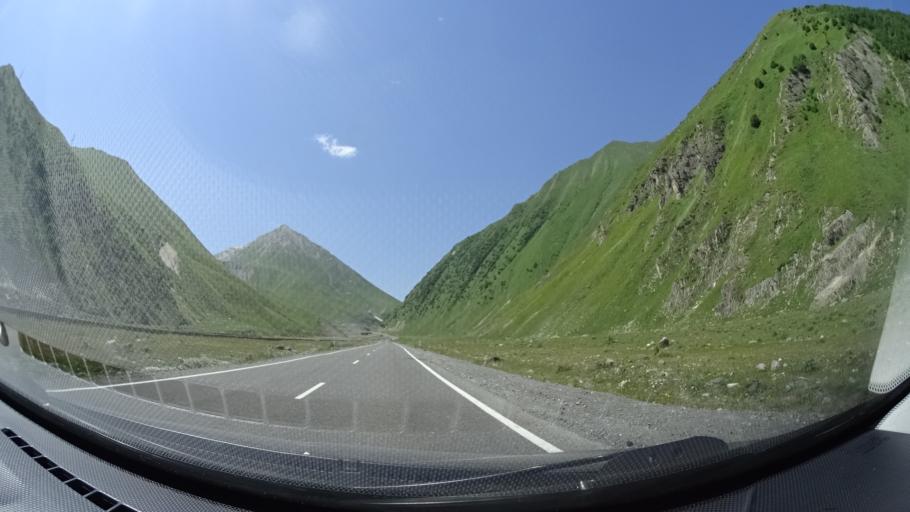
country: GE
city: Gudauri
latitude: 42.5539
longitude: 44.4979
